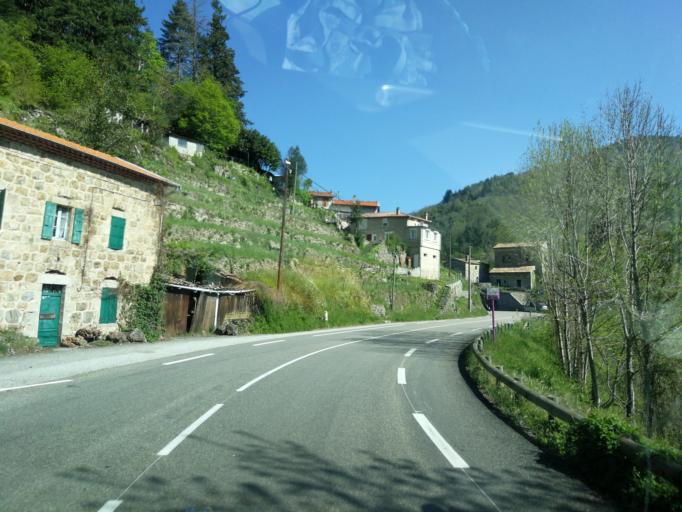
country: FR
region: Rhone-Alpes
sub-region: Departement de l'Ardeche
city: Le Cheylard
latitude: 44.8906
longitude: 4.4924
